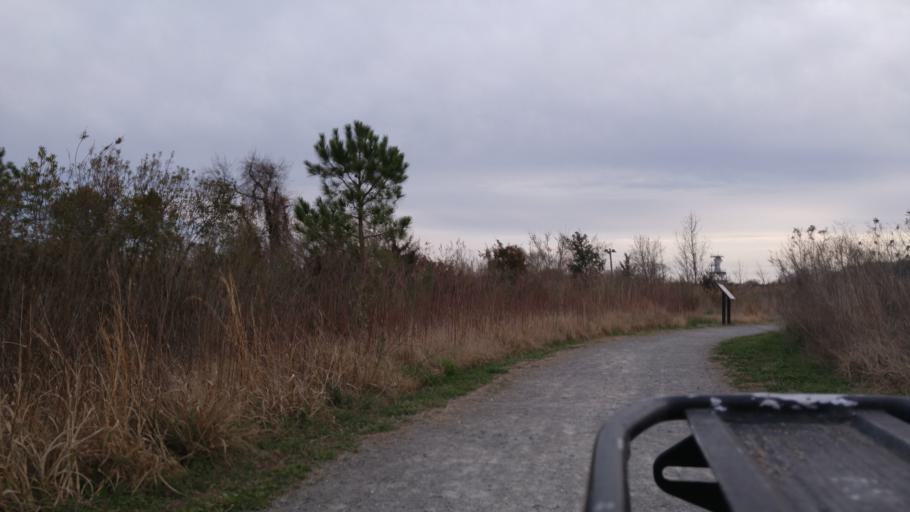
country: US
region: Virginia
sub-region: City of Chesapeake
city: Chesapeake
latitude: 36.7979
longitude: -76.3052
